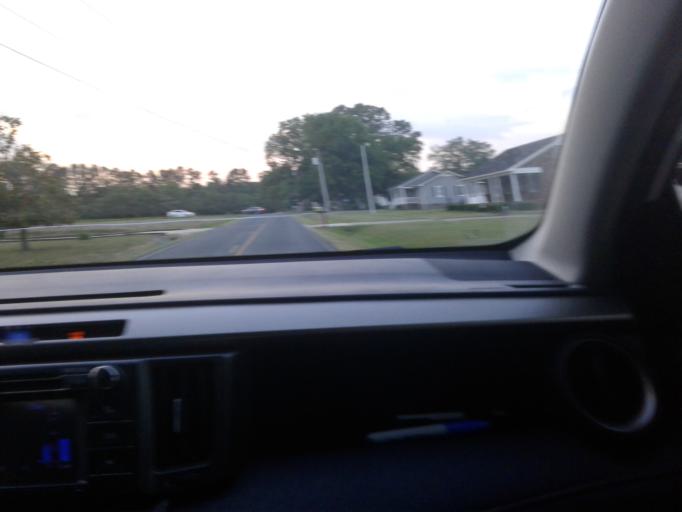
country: US
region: North Carolina
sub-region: Harnett County
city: Dunn
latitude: 35.3423
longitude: -78.5778
